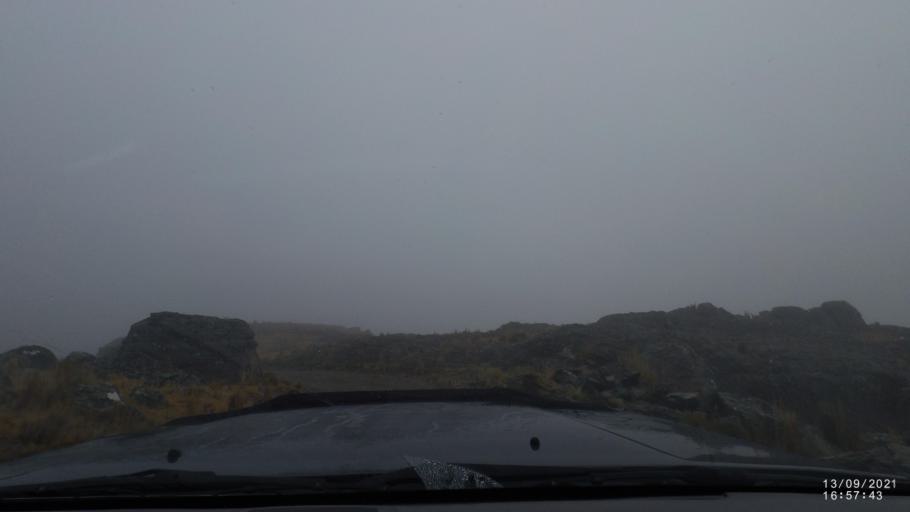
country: BO
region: Cochabamba
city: Colomi
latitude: -17.3065
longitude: -65.7161
